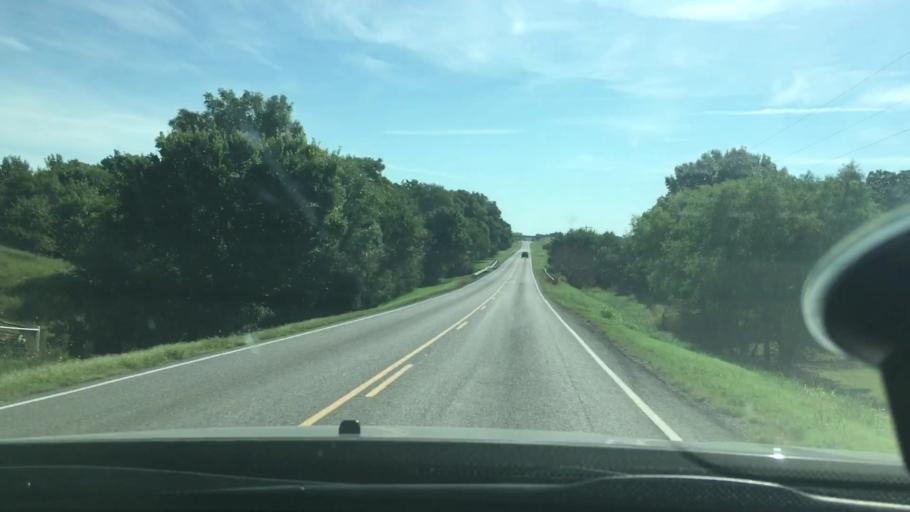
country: US
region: Oklahoma
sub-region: Carter County
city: Ardmore
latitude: 34.3327
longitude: -97.1652
